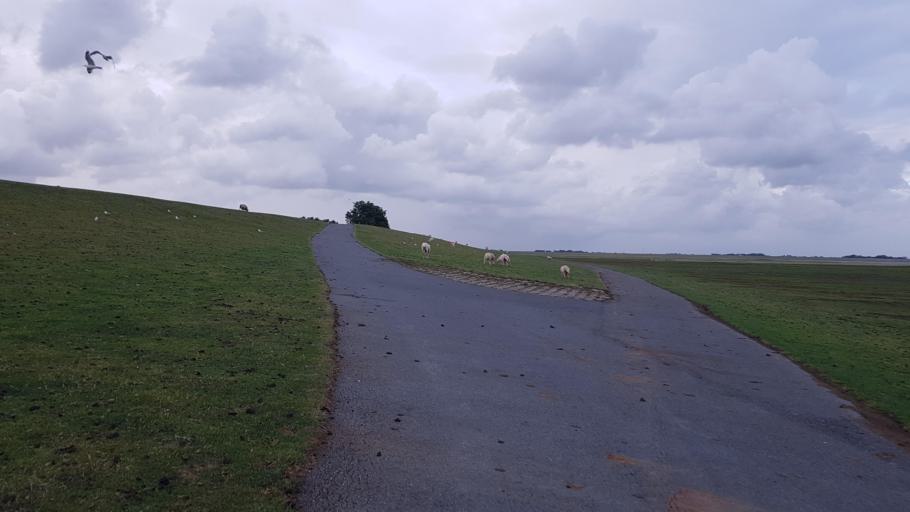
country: DE
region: Schleswig-Holstein
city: Tating
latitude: 54.2817
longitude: 8.6915
